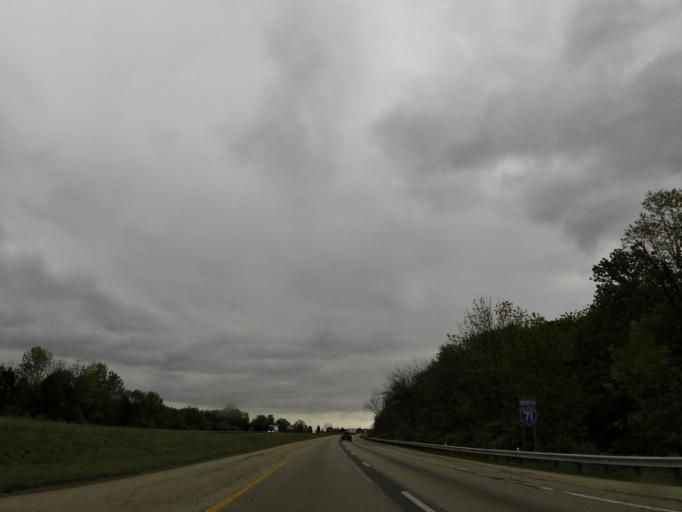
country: US
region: Ohio
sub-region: Warren County
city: Waynesville
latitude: 39.4344
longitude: -84.0711
